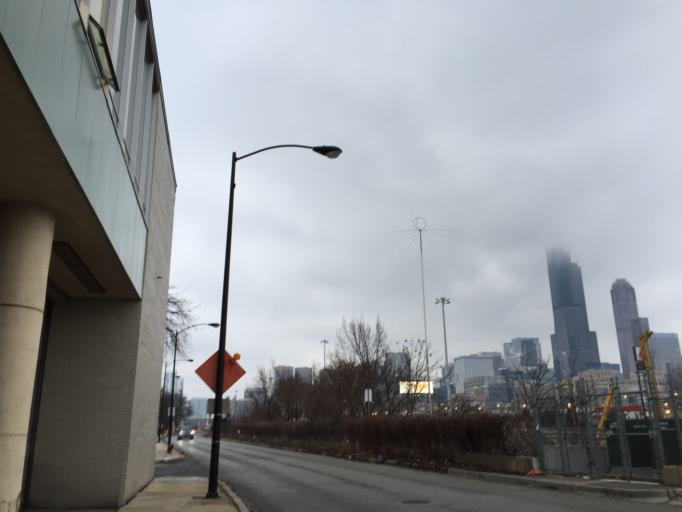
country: US
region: Illinois
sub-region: Cook County
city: Chicago
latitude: 41.8679
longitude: -87.6453
